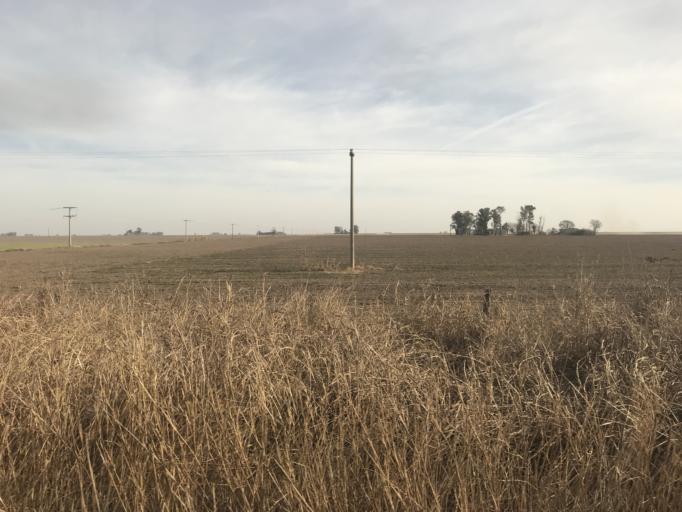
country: AR
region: Cordoba
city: Laguna Larga
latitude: -31.7516
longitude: -63.8252
